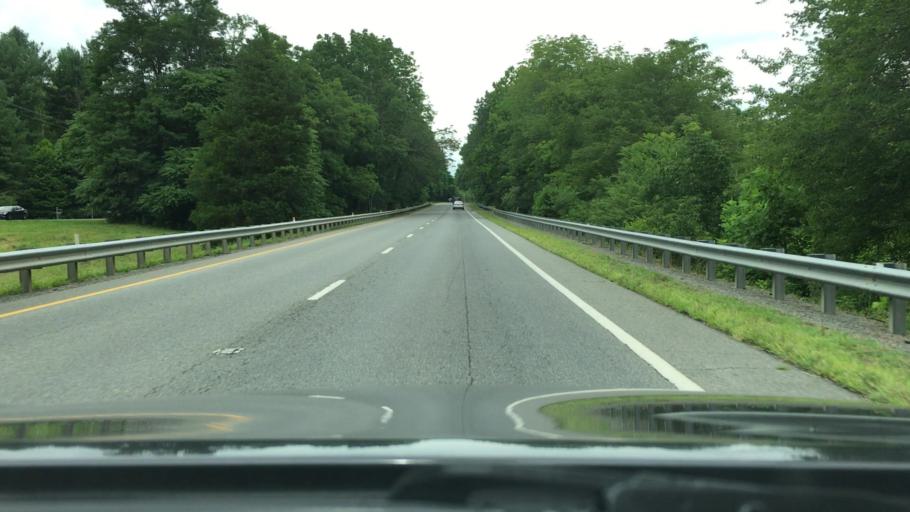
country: US
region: Virginia
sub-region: Albemarle County
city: Crozet
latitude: 37.9181
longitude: -78.6838
